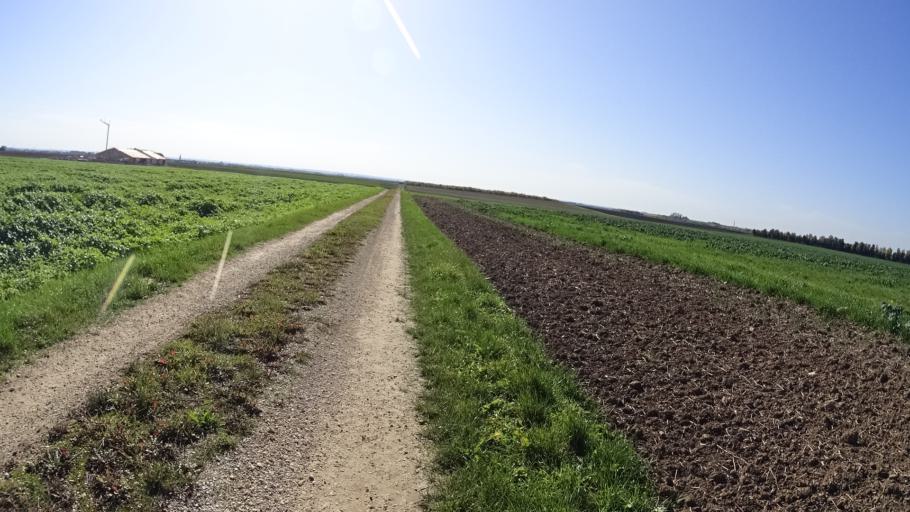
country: DE
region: Bavaria
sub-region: Upper Bavaria
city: Gaimersheim
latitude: 48.8330
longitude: 11.3510
